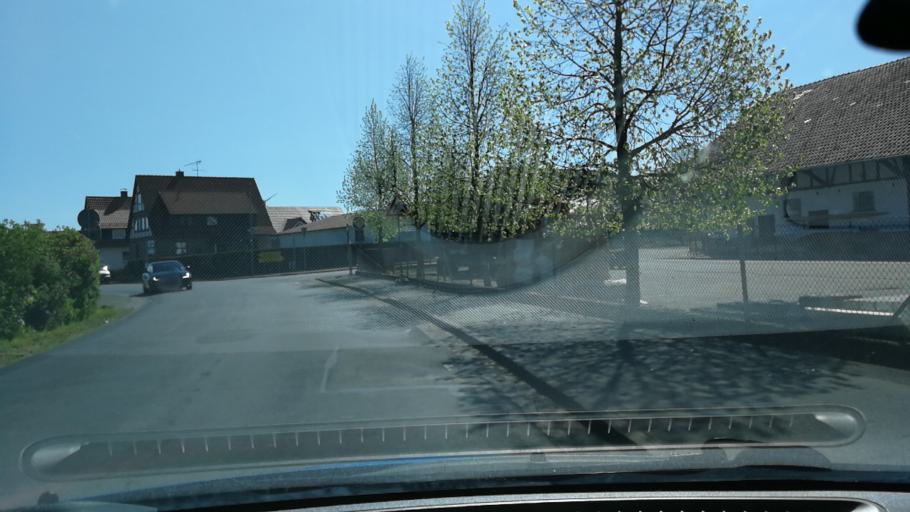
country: DE
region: Lower Saxony
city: Buhren
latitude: 51.5202
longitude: 9.7066
